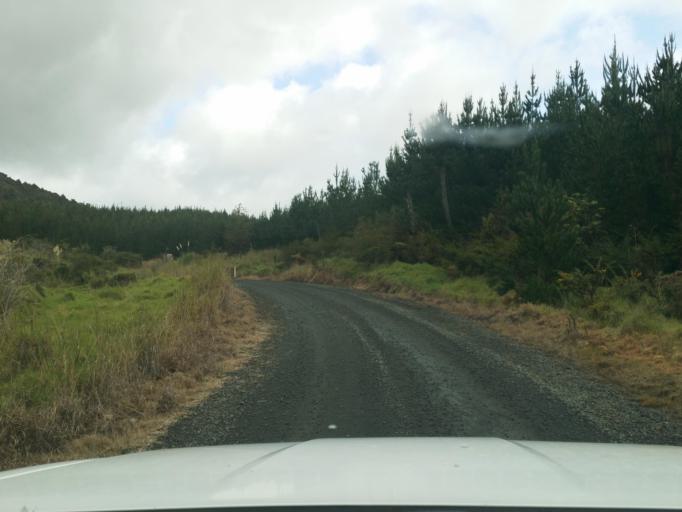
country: NZ
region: Northland
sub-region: Kaipara District
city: Dargaville
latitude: -35.7815
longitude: 173.7773
